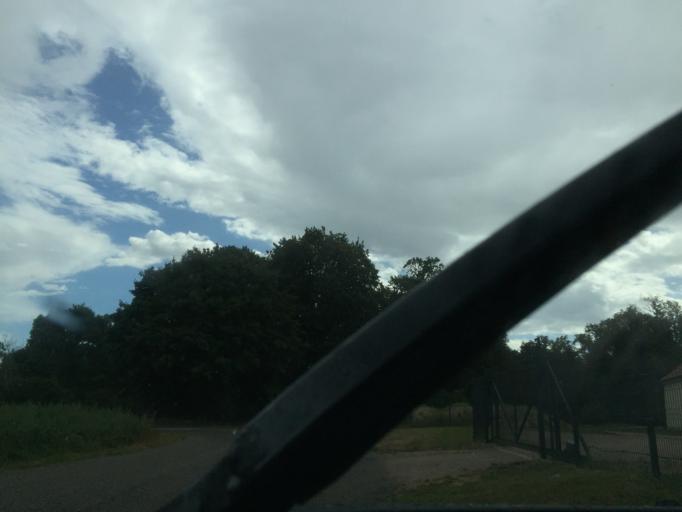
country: LT
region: Siauliu apskritis
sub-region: Joniskis
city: Joniskis
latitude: 56.3446
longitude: 23.5488
